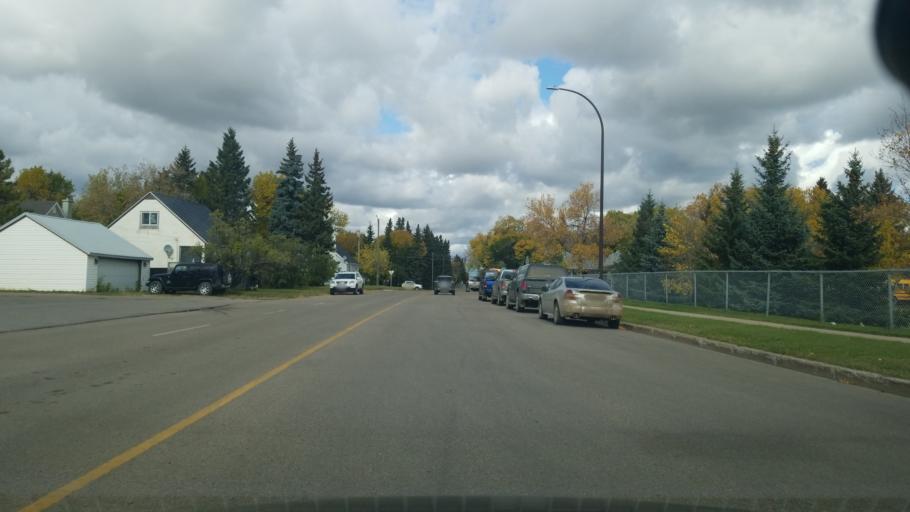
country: CA
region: Saskatchewan
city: Lloydminster
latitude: 53.2782
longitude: -110.0156
